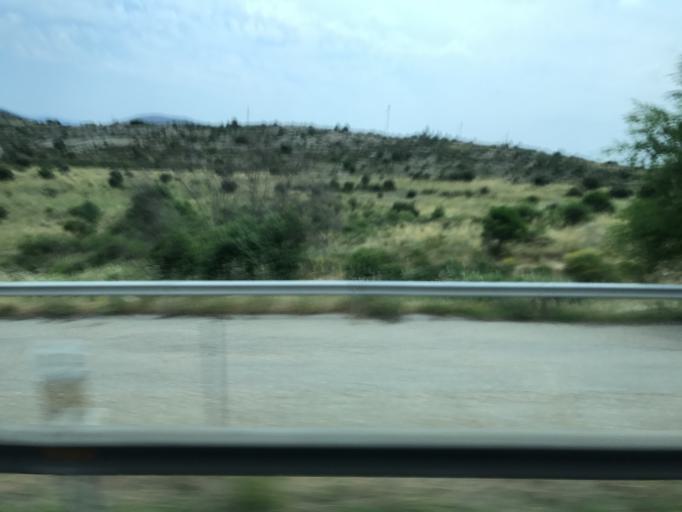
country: ES
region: Madrid
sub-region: Provincia de Madrid
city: La Cabrera
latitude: 40.8807
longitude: -3.5988
